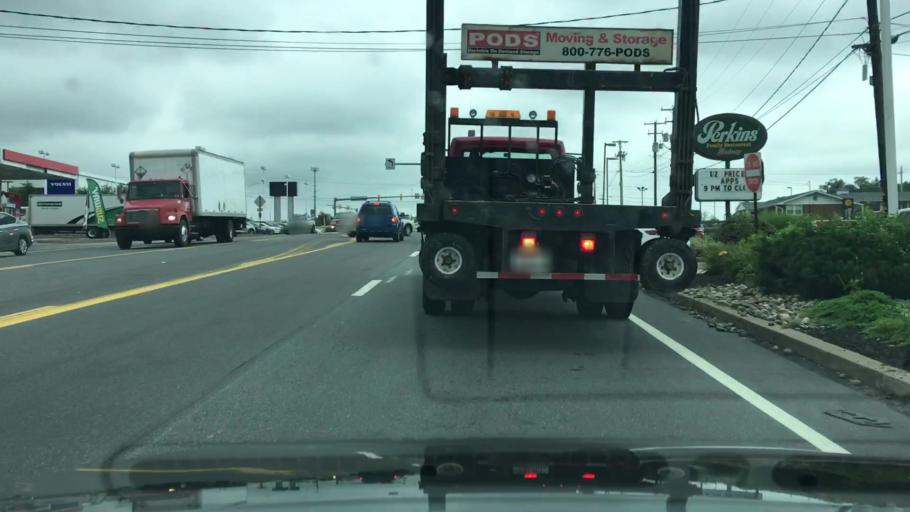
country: US
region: Pennsylvania
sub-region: Luzerne County
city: Hughestown
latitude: 41.3069
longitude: -75.7637
